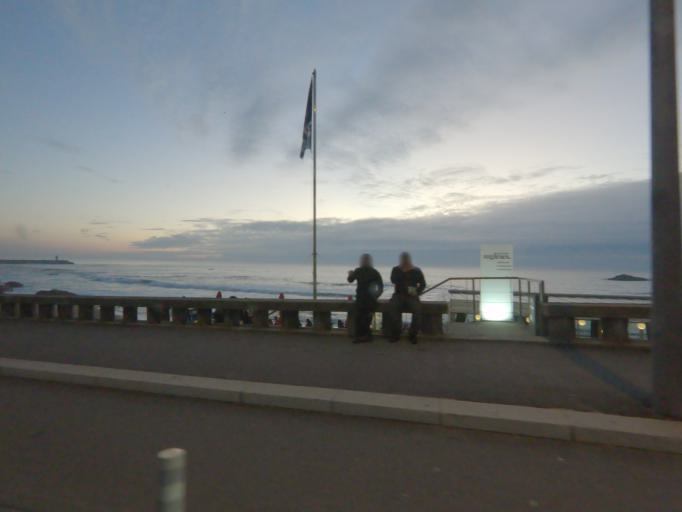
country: PT
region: Porto
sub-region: Matosinhos
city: Matosinhos
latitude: 41.1524
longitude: -8.6782
